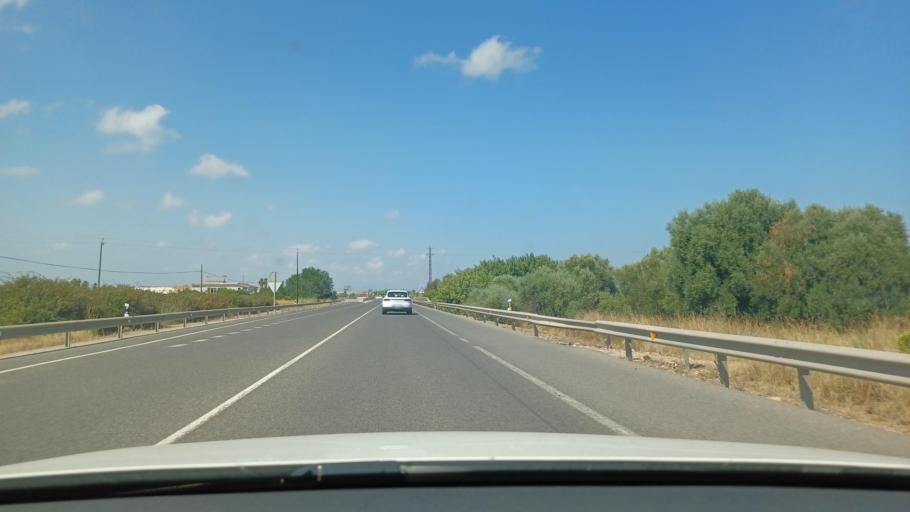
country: ES
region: Valencia
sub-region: Provincia de Castello
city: Moncofar
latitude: 39.8099
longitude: -0.1697
